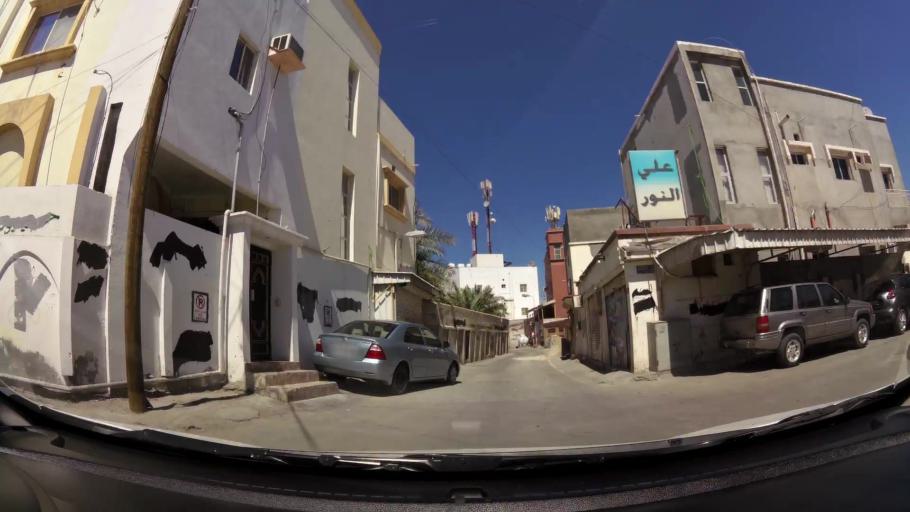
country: BH
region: Muharraq
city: Al Muharraq
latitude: 26.2837
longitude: 50.6240
